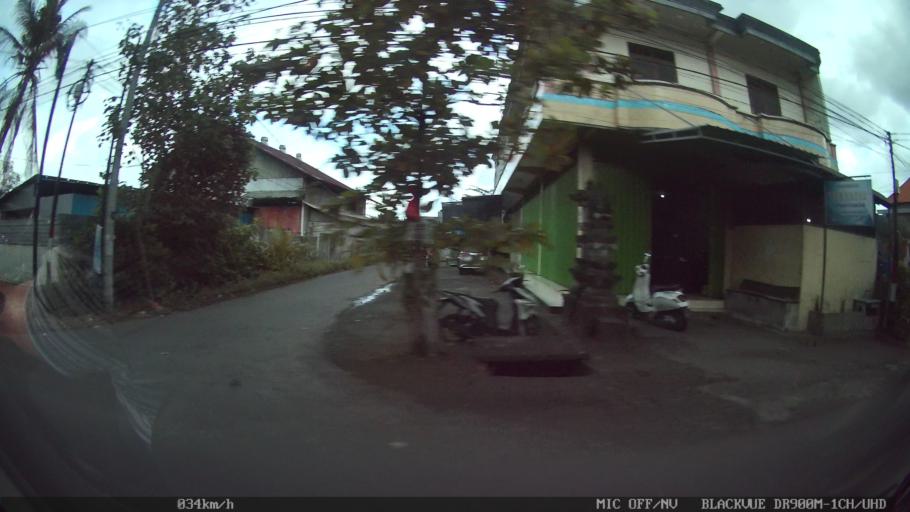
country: ID
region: Bali
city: Banjar Tegal Belodan
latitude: -8.5439
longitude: 115.1212
